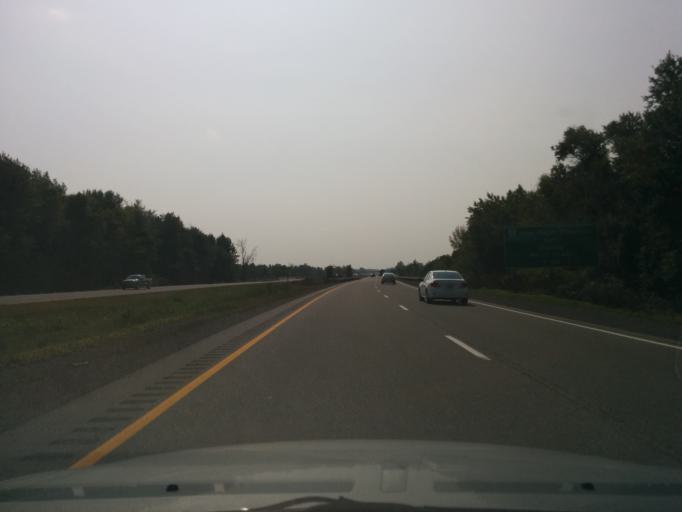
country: CA
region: Ontario
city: Bells Corners
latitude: 45.1589
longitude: -75.6862
